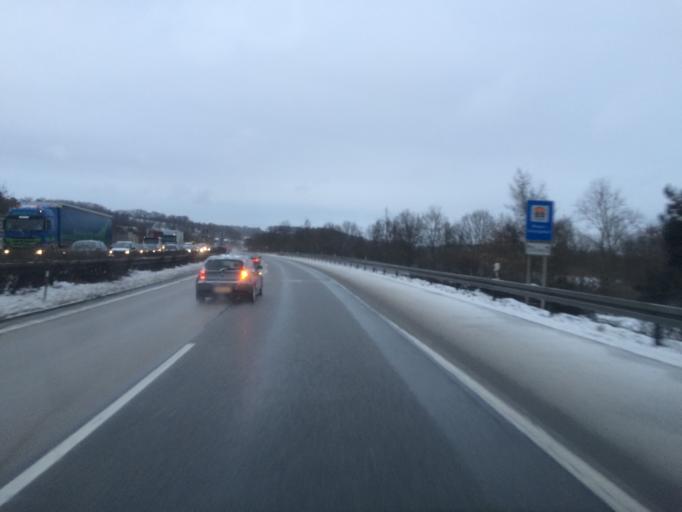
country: DE
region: Bavaria
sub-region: Upper Palatinate
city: Lappersdorf
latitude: 49.0452
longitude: 12.0958
